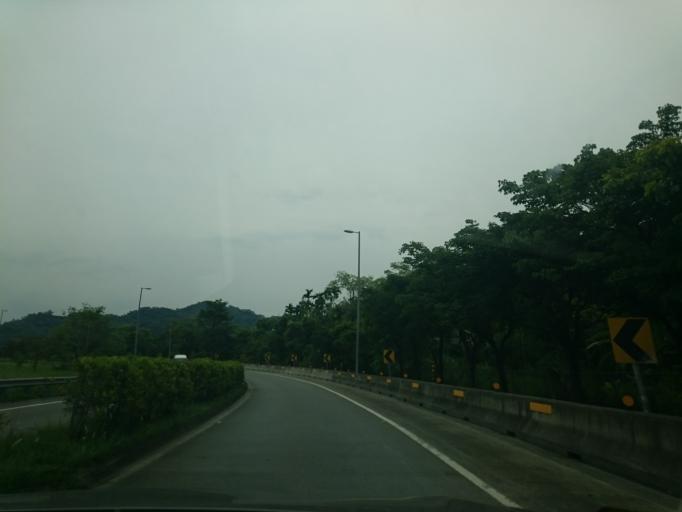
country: TW
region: Taiwan
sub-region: Nantou
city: Nantou
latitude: 23.8525
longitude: 120.7030
